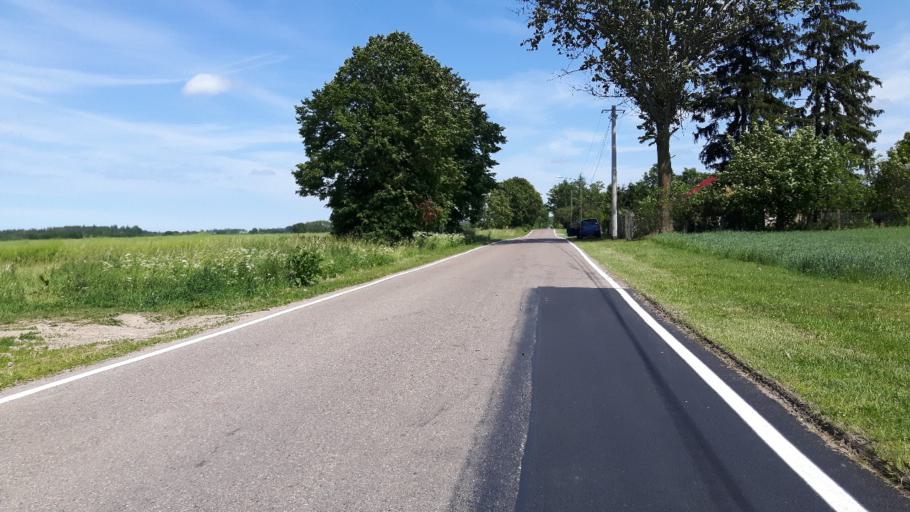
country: PL
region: Pomeranian Voivodeship
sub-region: Powiat wejherowski
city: Gniewino
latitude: 54.7241
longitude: 17.9662
